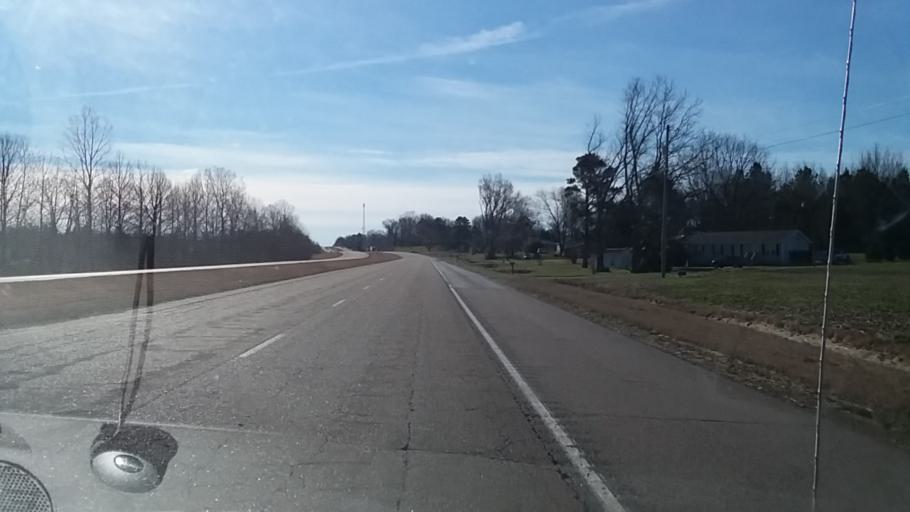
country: US
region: Tennessee
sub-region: Lauderdale County
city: Halls
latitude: 35.9197
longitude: -89.2754
